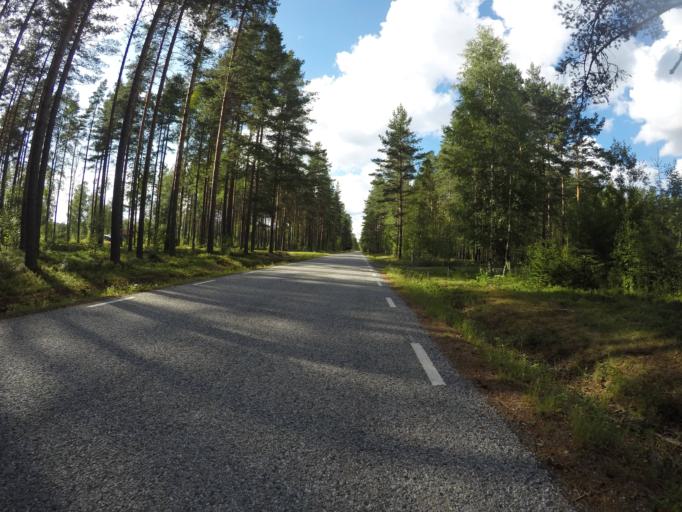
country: SE
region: OErebro
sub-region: Hallefors Kommun
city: Haellefors
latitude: 59.9075
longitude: 14.5513
